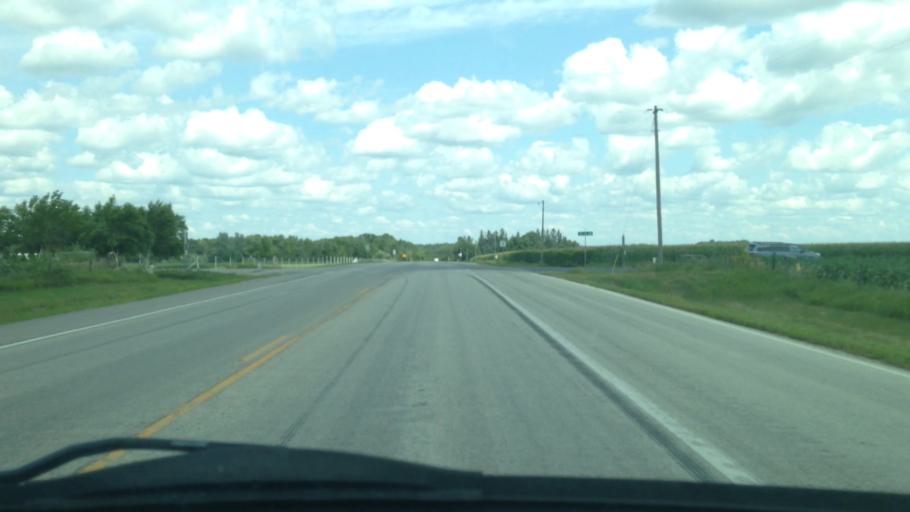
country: US
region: Minnesota
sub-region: Olmsted County
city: Rochester
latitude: 43.9637
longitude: -92.5183
